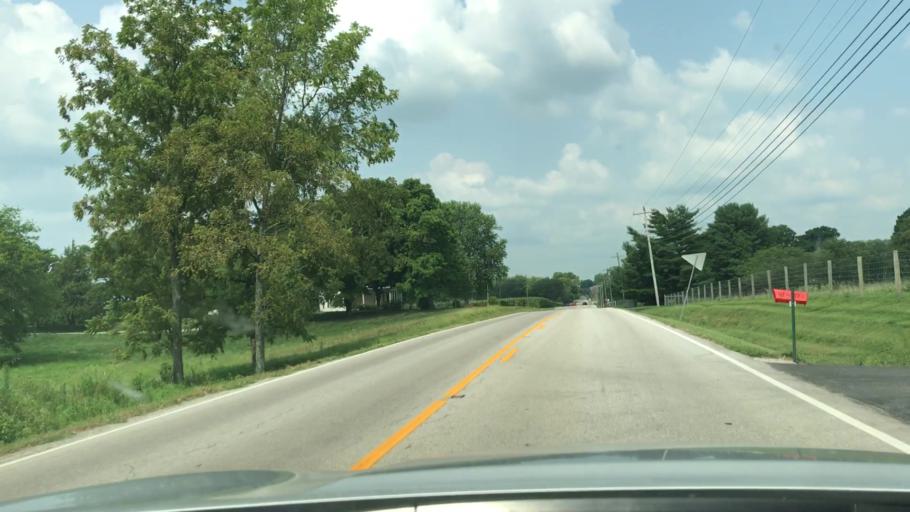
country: US
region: Kentucky
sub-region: Todd County
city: Elkton
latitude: 36.8065
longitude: -87.1345
